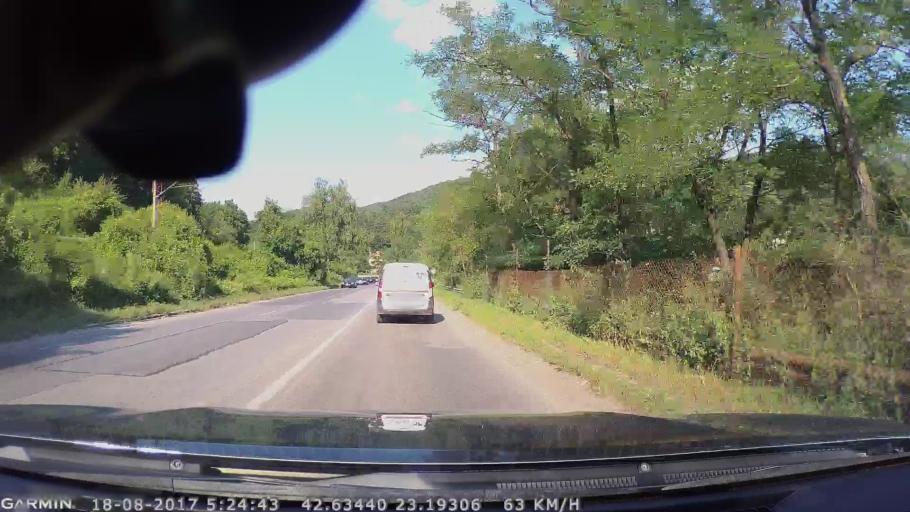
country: BG
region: Kyustendil
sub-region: Obshtina Bobovdol
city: Bobovdol
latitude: 42.3982
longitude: 23.1208
